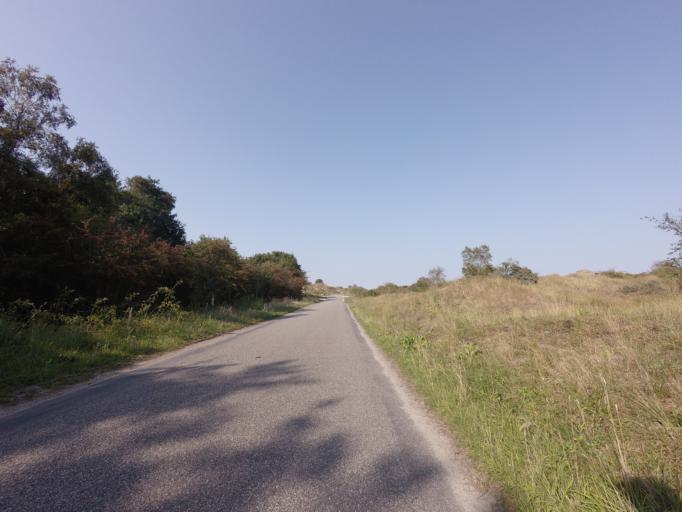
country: NL
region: Friesland
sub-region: Gemeente Schiermonnikoog
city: Schiermonnikoog
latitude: 53.4861
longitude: 6.1791
